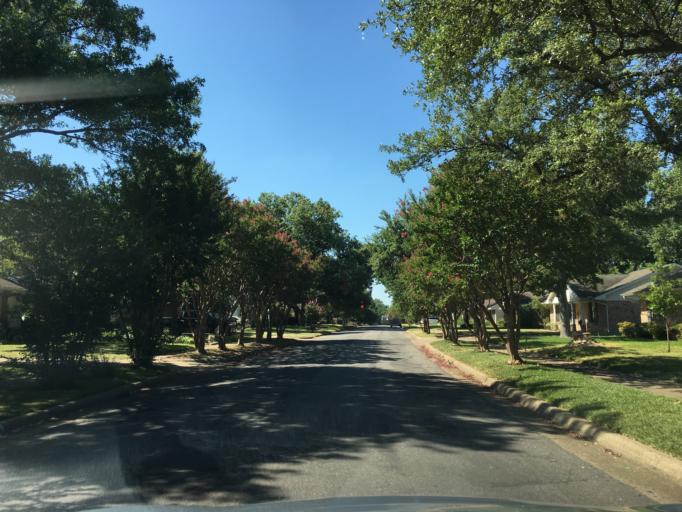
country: US
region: Texas
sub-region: Dallas County
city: Garland
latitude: 32.8673
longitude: -96.6940
